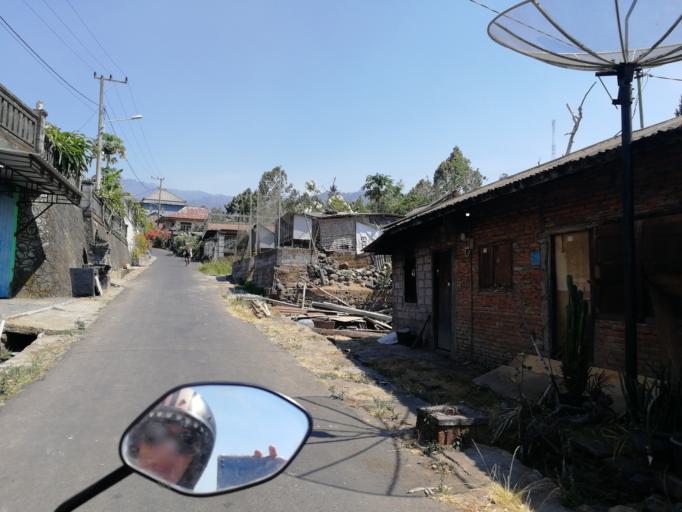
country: ID
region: Bali
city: Banjar Kedisan
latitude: -8.1505
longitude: 115.3068
